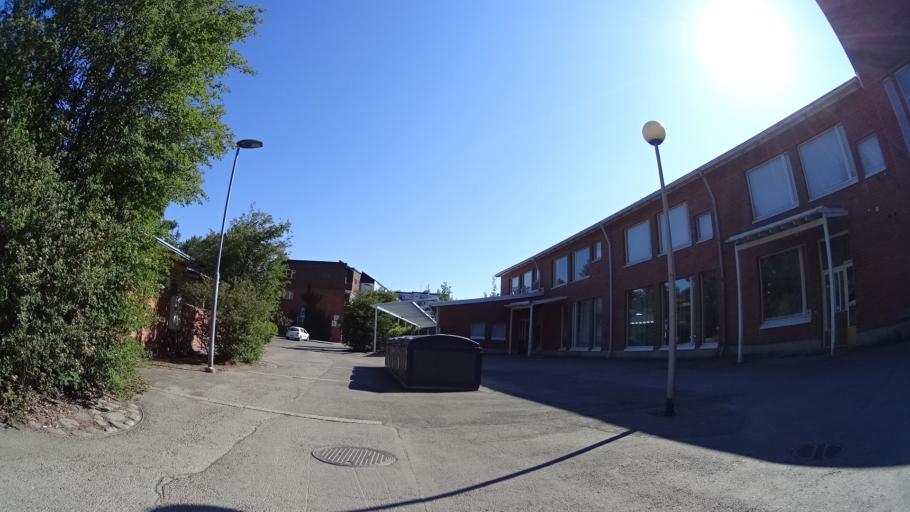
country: FI
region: Uusimaa
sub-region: Helsinki
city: Teekkarikylae
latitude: 60.2462
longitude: 24.8596
